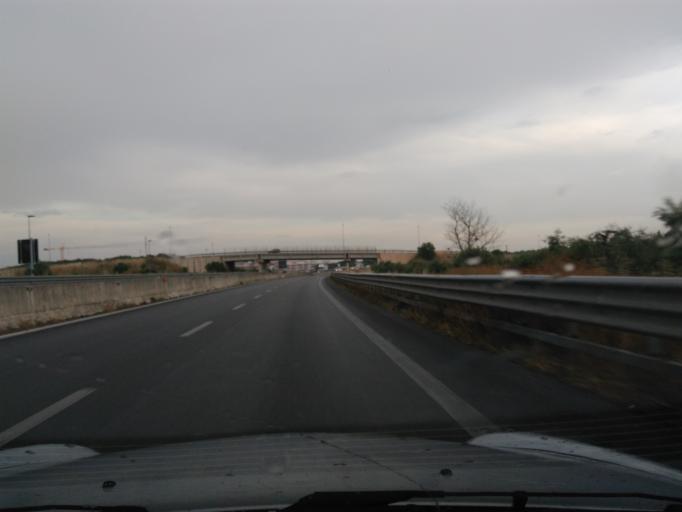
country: IT
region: Apulia
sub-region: Provincia di Bari
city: Molfetta
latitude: 41.1968
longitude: 16.5791
